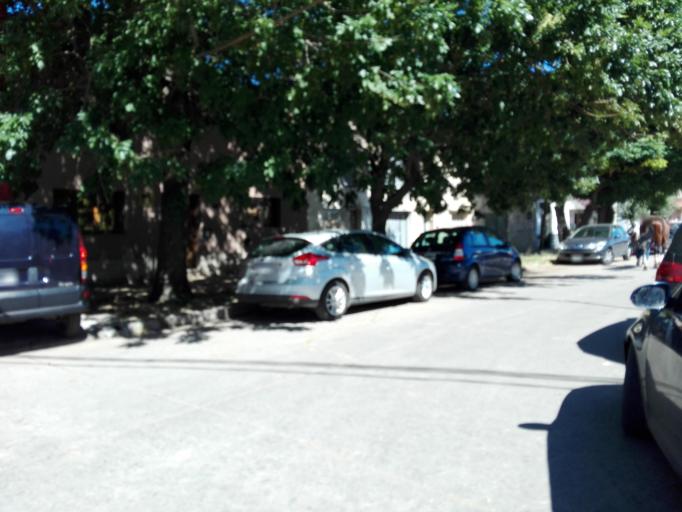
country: AR
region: Buenos Aires
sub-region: Partido de La Plata
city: La Plata
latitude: -34.8976
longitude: -57.9471
